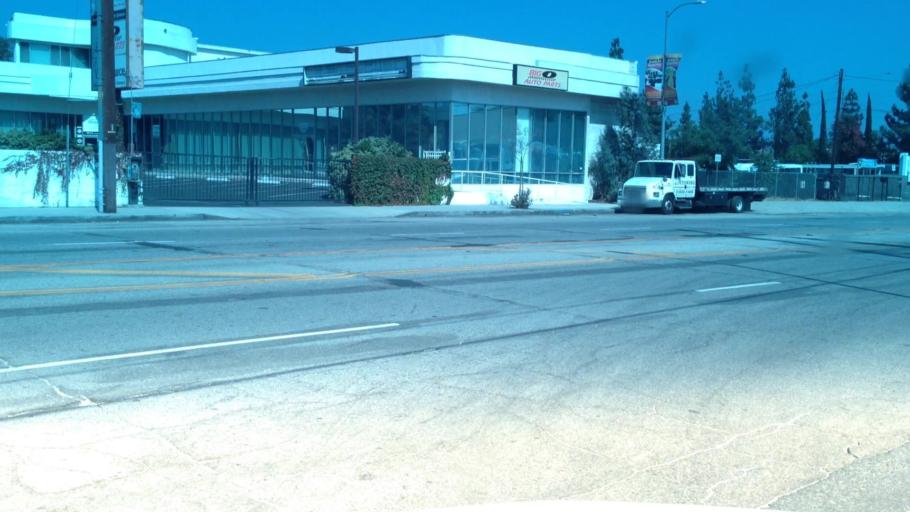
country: US
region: California
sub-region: Los Angeles County
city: San Fernando
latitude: 34.2334
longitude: -118.4054
